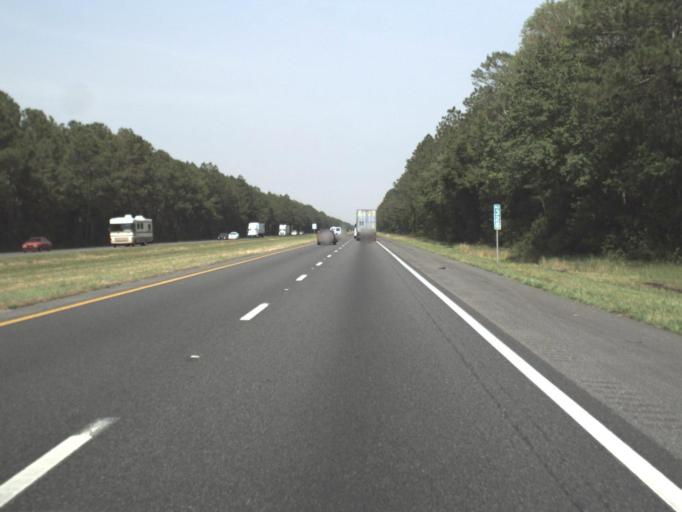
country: US
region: Florida
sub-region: Baker County
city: Macclenny
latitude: 30.2444
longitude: -82.2406
